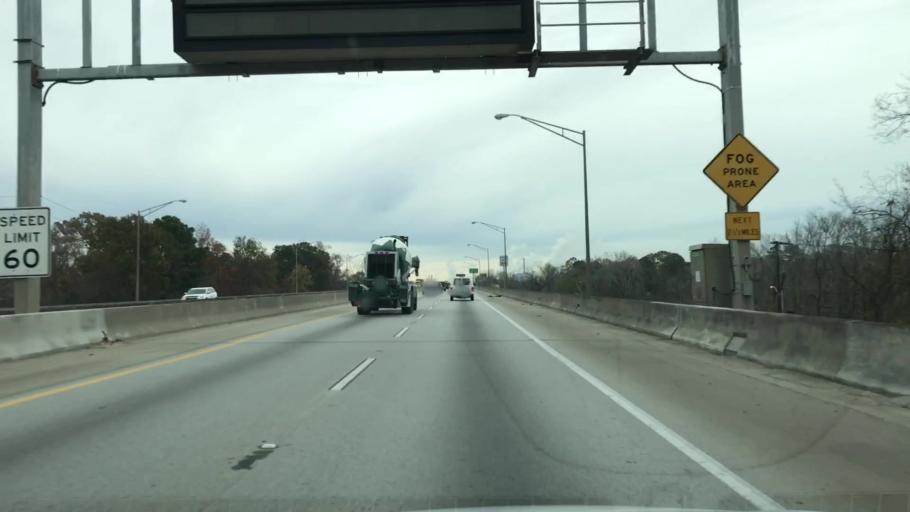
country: US
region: South Carolina
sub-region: Berkeley County
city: Hanahan
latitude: 32.8932
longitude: -80.0013
